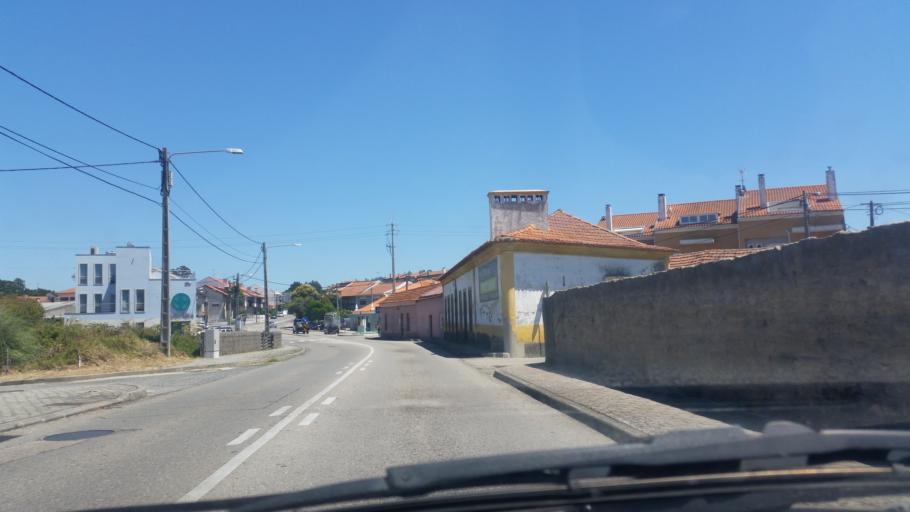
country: PT
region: Aveiro
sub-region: Aveiro
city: Aveiro
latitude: 40.6430
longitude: -8.6231
